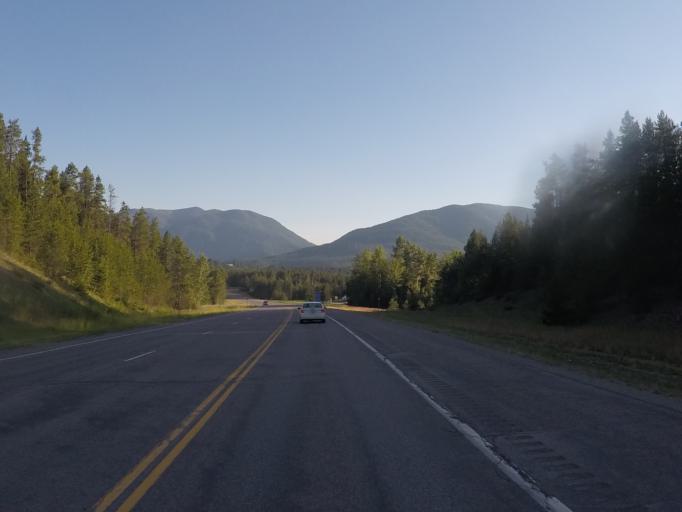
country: US
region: Montana
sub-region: Flathead County
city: Columbia Falls
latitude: 48.4434
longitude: -114.0379
